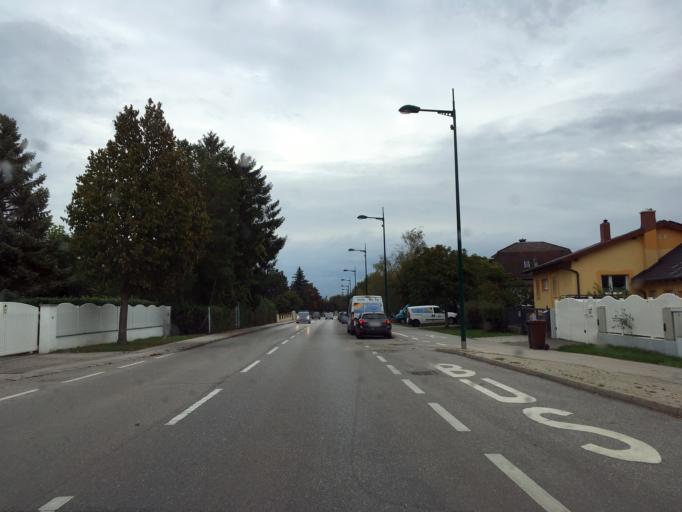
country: AT
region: Lower Austria
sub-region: Politischer Bezirk Modling
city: Maria Enzersdorf
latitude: 48.0988
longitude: 16.2957
